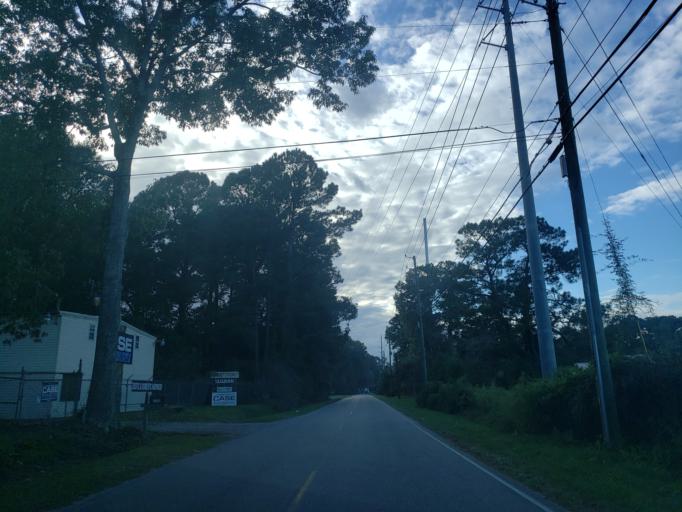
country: US
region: Georgia
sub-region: Chatham County
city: Georgetown
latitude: 31.9903
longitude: -81.2294
